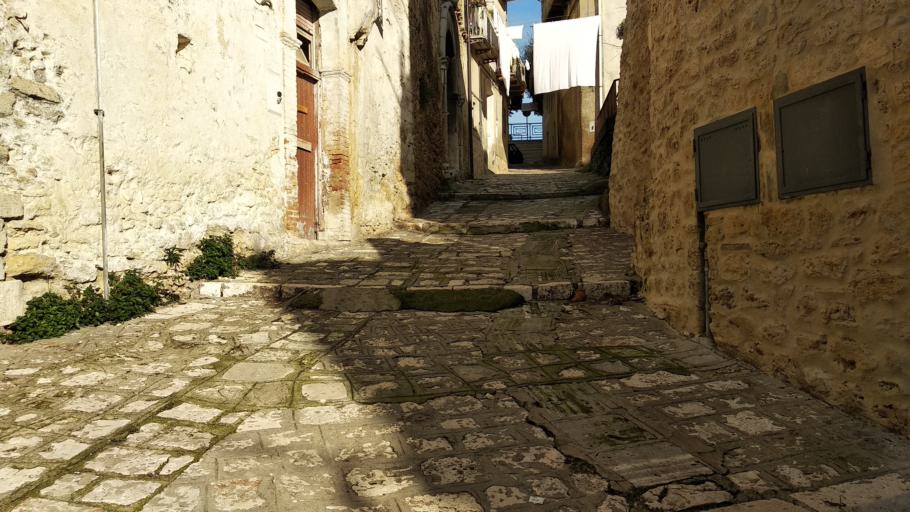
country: IT
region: Basilicate
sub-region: Provincia di Matera
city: Tricarico
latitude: 40.6225
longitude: 16.1443
